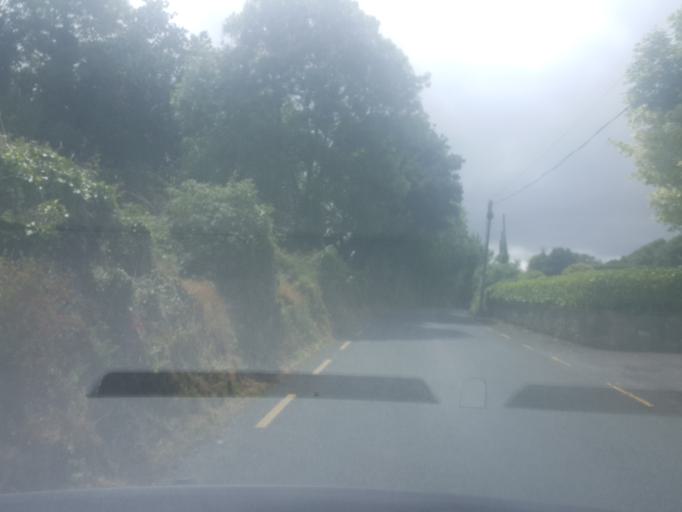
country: IE
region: Munster
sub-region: Ciarrai
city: Cill Airne
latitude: 52.0911
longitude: -9.4792
